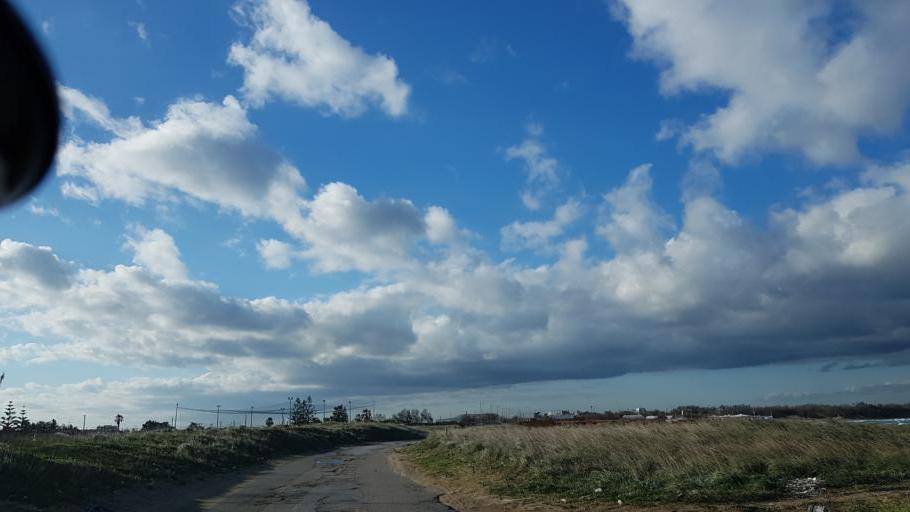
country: IT
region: Apulia
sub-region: Provincia di Brindisi
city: Materdomini
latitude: 40.6824
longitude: 17.9354
